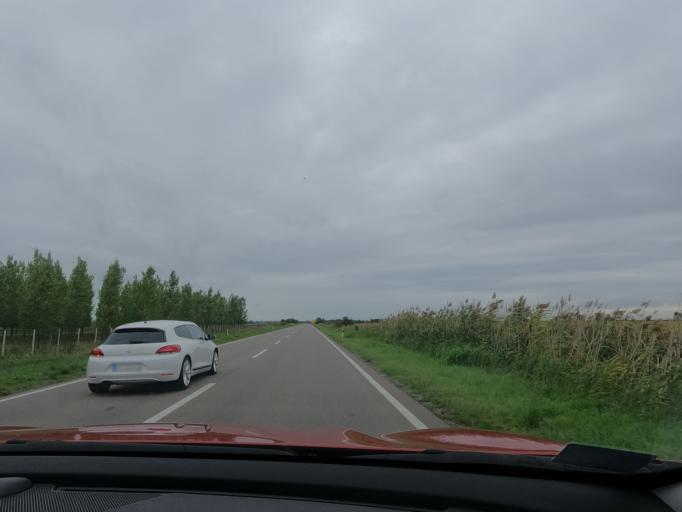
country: RS
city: Basaid
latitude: 45.6655
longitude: 20.4213
